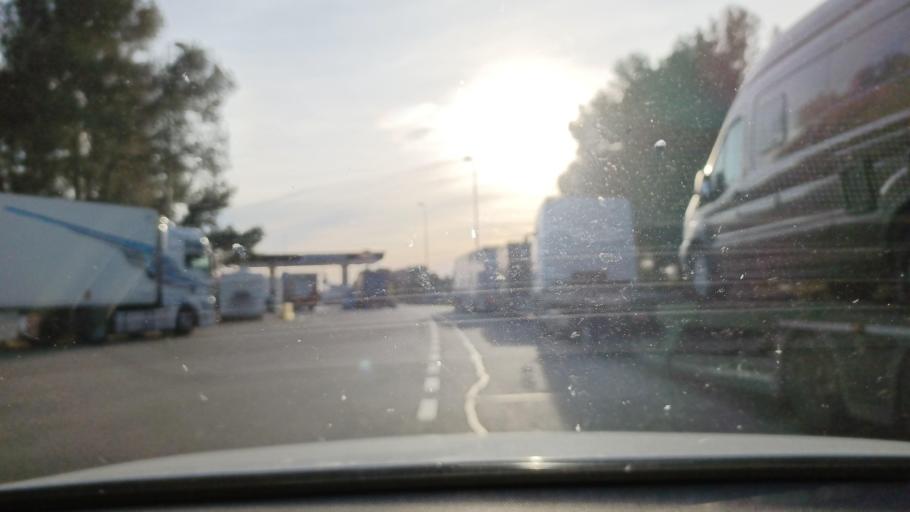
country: ES
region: Catalonia
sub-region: Provincia de Tarragona
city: Sant Jaume dels Domenys
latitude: 41.2897
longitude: 1.5903
